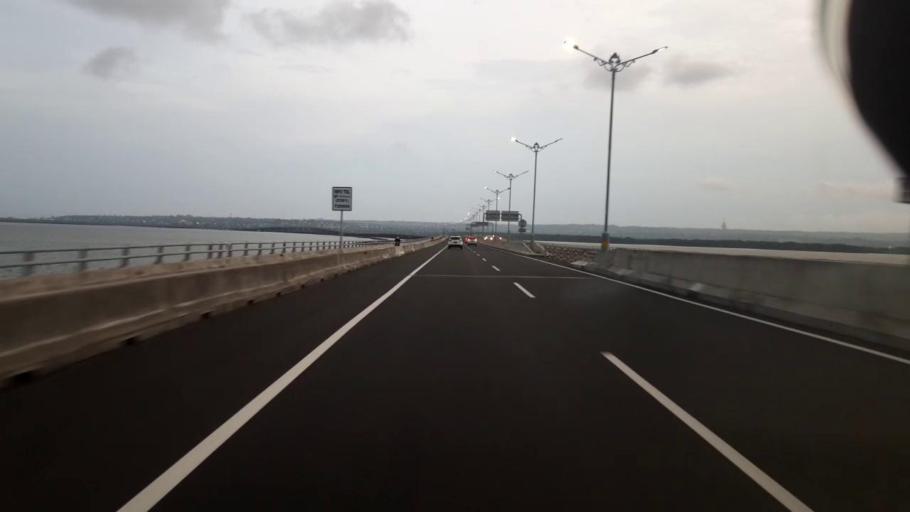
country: ID
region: Bali
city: Kelanabian
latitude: -8.7531
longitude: 115.1954
